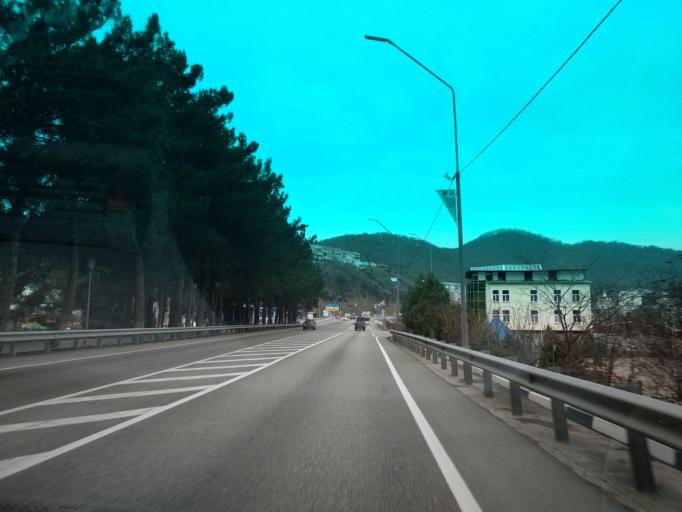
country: RU
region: Krasnodarskiy
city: Ol'ginka
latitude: 44.1980
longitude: 38.8901
